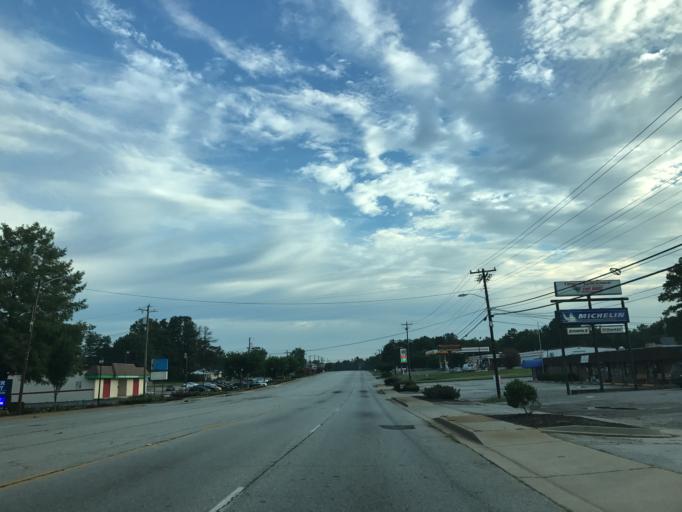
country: US
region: South Carolina
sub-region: Greenville County
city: Mauldin
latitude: 34.7867
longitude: -82.3132
